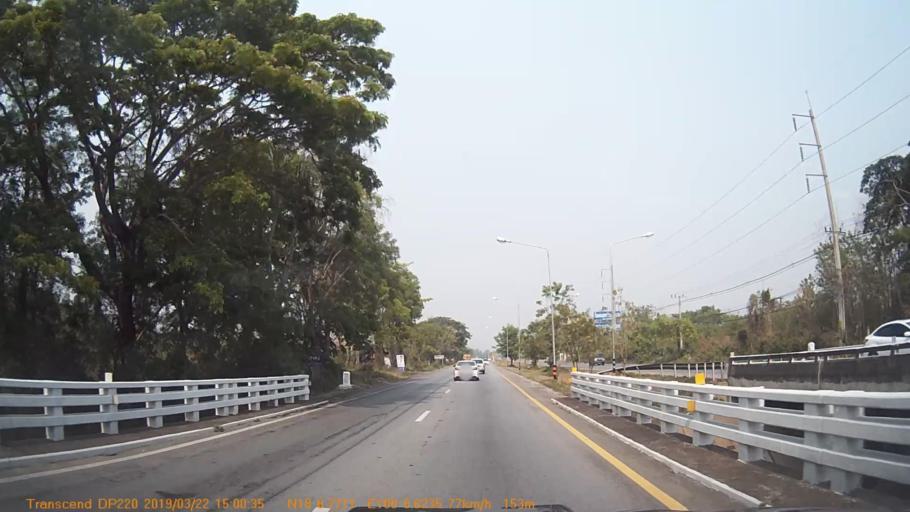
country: TH
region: Phrae
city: Phrae
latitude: 18.1131
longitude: 100.1442
